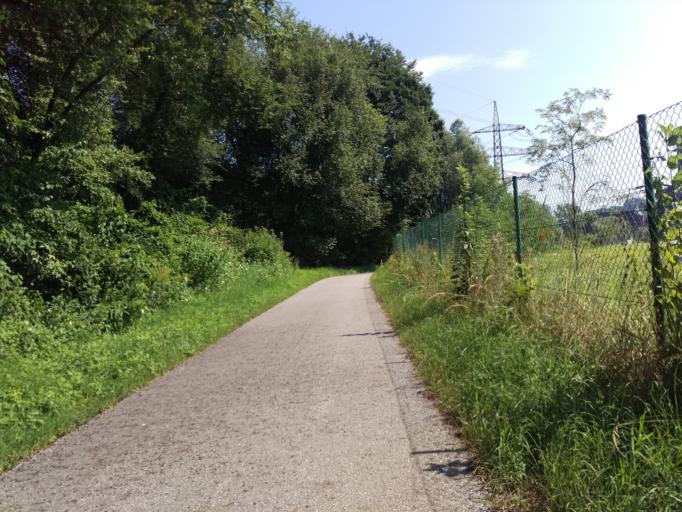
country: AT
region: Styria
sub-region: Politischer Bezirk Graz-Umgebung
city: Werndorf
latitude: 46.9092
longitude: 15.4821
